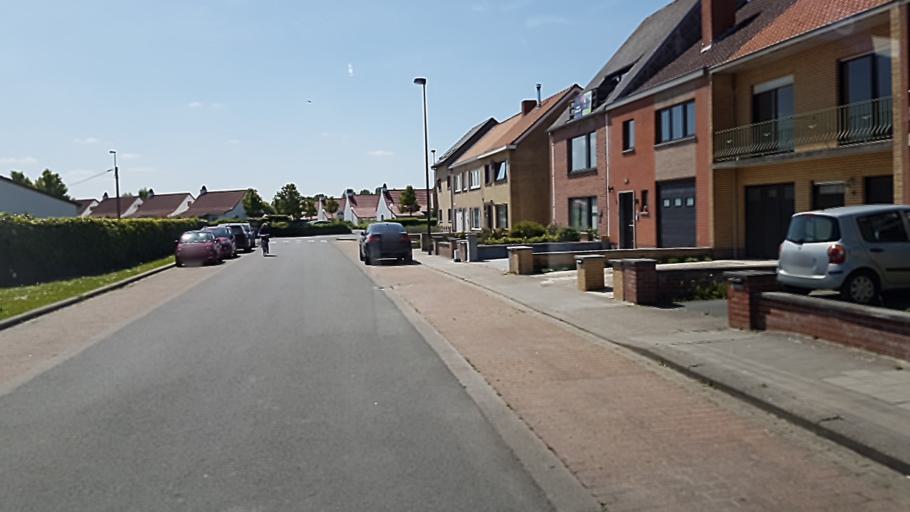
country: BE
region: Flanders
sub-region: Provincie West-Vlaanderen
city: De Haan
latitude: 51.2667
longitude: 3.0346
